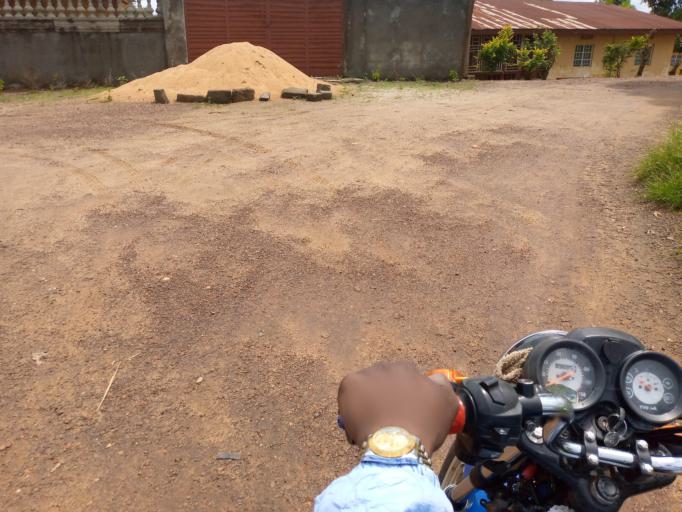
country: SL
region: Eastern Province
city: Kenema
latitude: 7.8788
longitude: -11.1667
